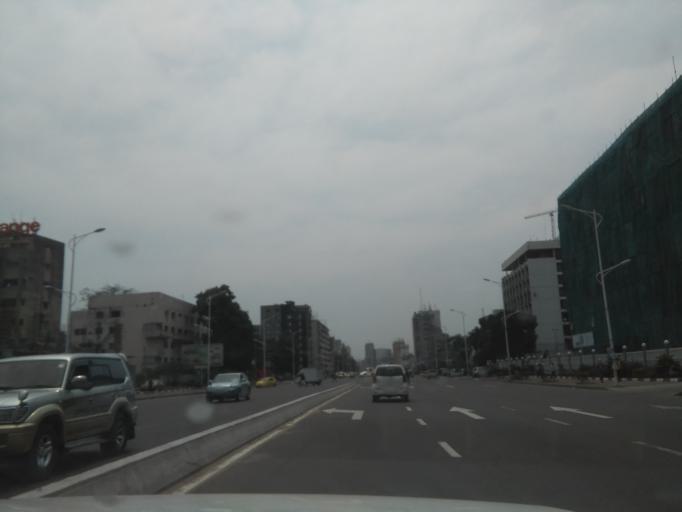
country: CD
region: Kinshasa
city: Kinshasa
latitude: -4.3070
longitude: 15.2955
